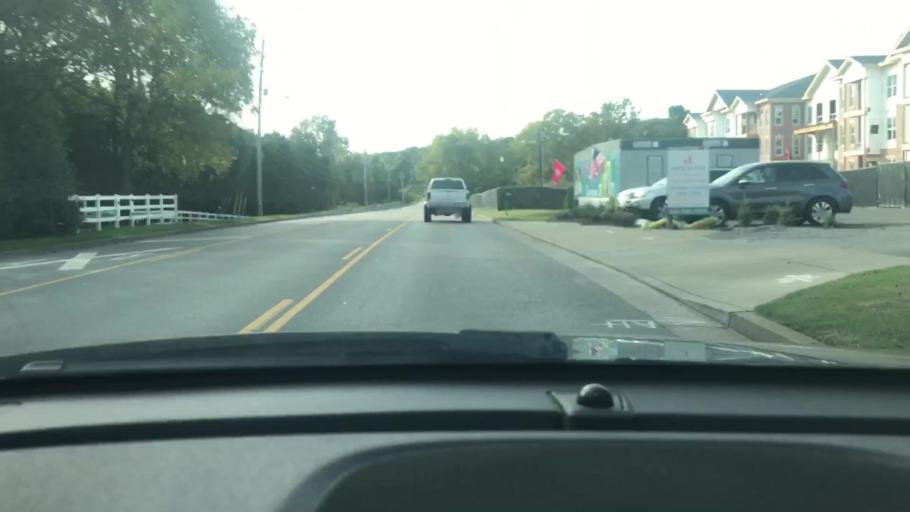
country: US
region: Tennessee
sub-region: Williamson County
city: Franklin
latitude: 35.9561
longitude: -86.8331
